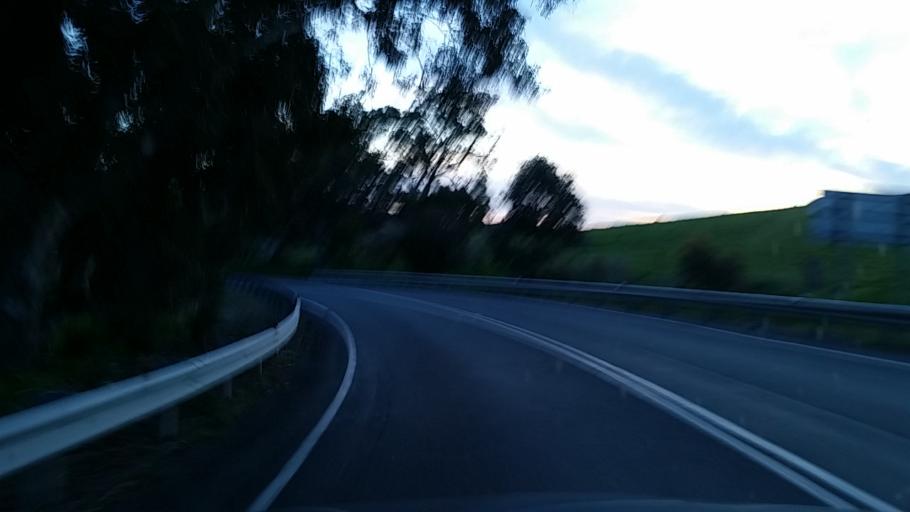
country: AU
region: South Australia
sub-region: Yankalilla
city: Normanville
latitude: -35.4557
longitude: 138.3551
